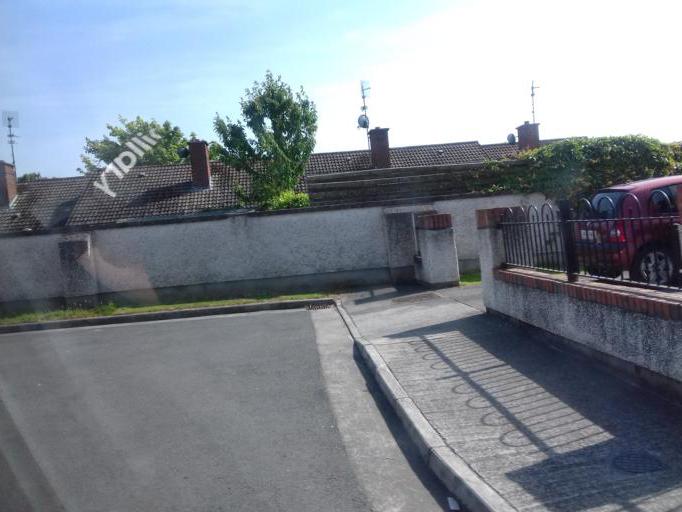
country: IE
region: Leinster
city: Lusk
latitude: 53.5282
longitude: -6.1751
